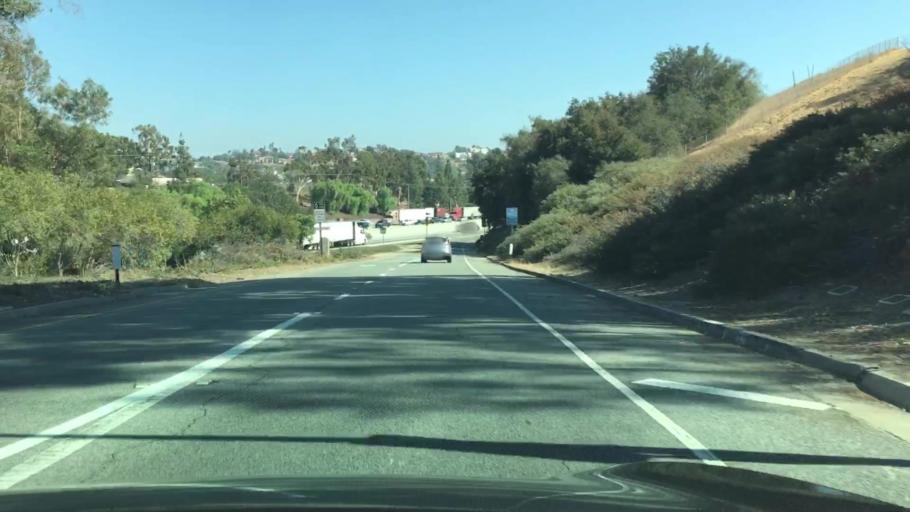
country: US
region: California
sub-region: Los Angeles County
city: Walnut
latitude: 33.9839
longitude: -117.8437
